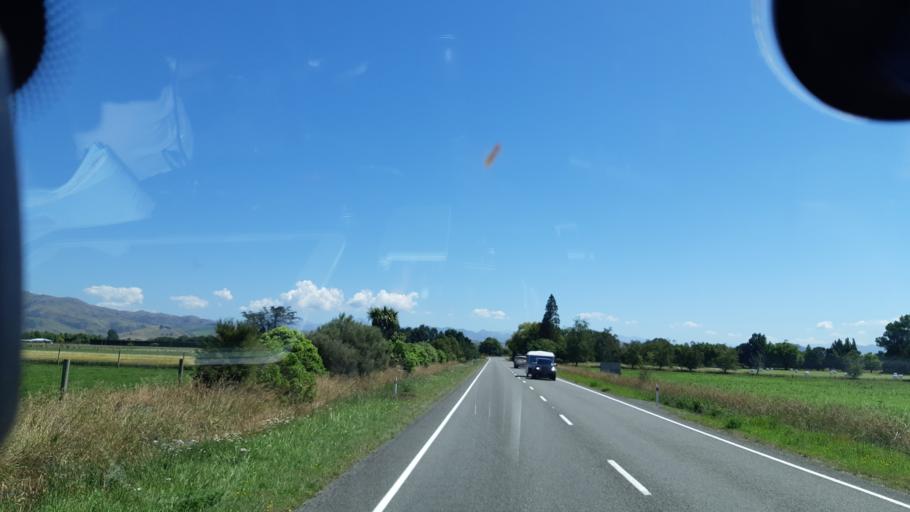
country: NZ
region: Canterbury
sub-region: Kaikoura District
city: Kaikoura
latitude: -42.7444
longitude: 173.2670
